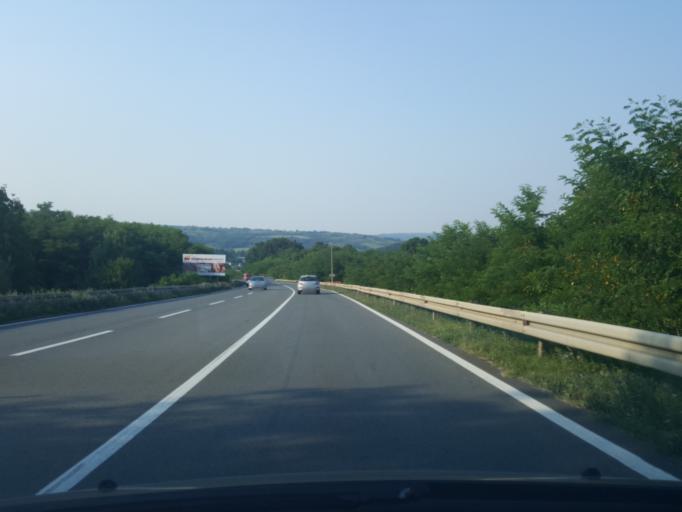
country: RS
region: Central Serbia
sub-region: Belgrade
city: Sopot
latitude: 44.5528
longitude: 20.6660
